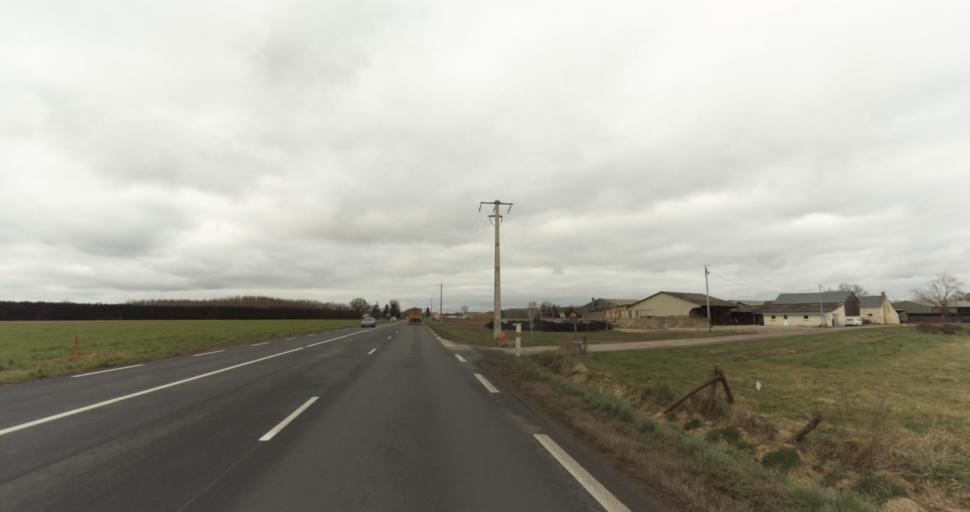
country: FR
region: Pays de la Loire
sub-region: Departement de Maine-et-Loire
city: Vivy
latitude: 47.3085
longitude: -0.0393
